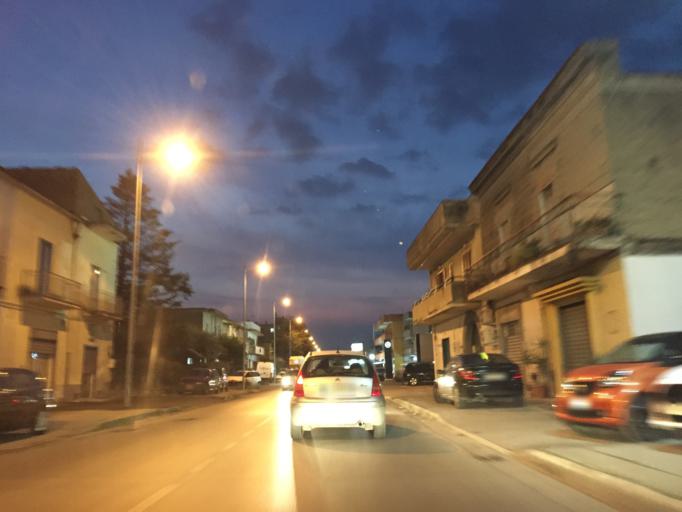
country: IT
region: Campania
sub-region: Provincia di Salerno
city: San Lorenzo
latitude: 40.7480
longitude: 14.5914
